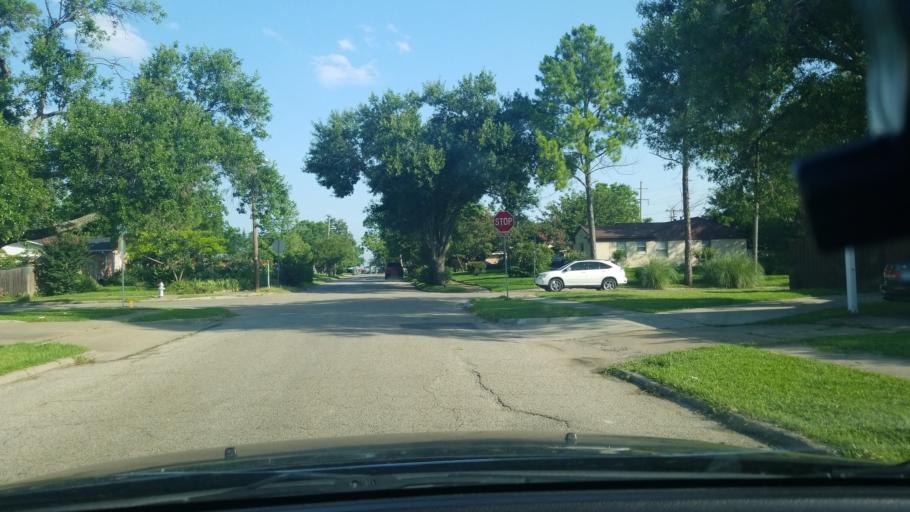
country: US
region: Texas
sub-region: Dallas County
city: Mesquite
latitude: 32.8131
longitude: -96.6376
